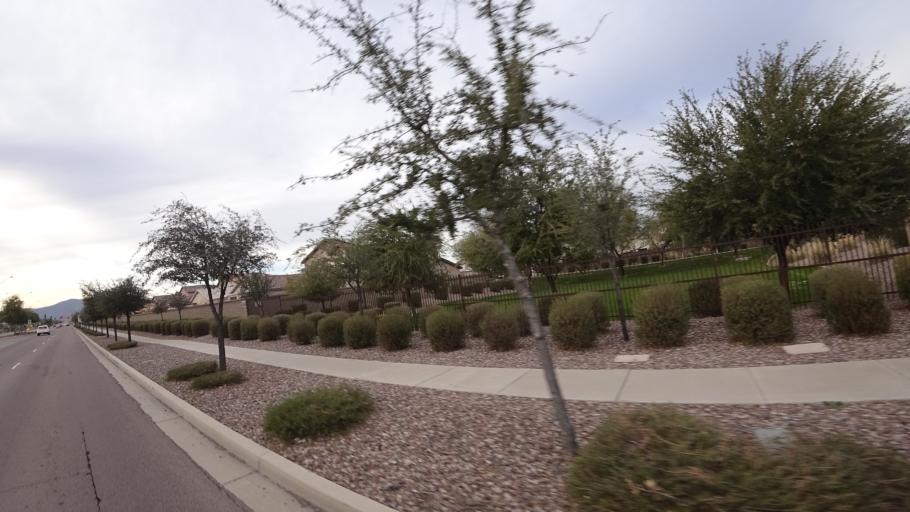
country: US
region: Arizona
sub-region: Maricopa County
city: Citrus Park
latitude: 33.6243
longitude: -112.4236
